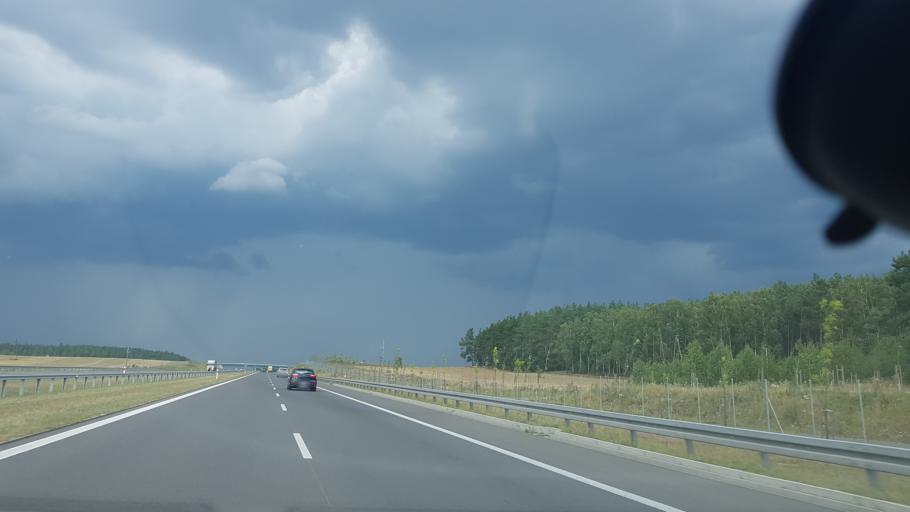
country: PL
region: Warmian-Masurian Voivodeship
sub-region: Powiat nidzicki
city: Nidzica
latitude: 53.3148
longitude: 20.4383
